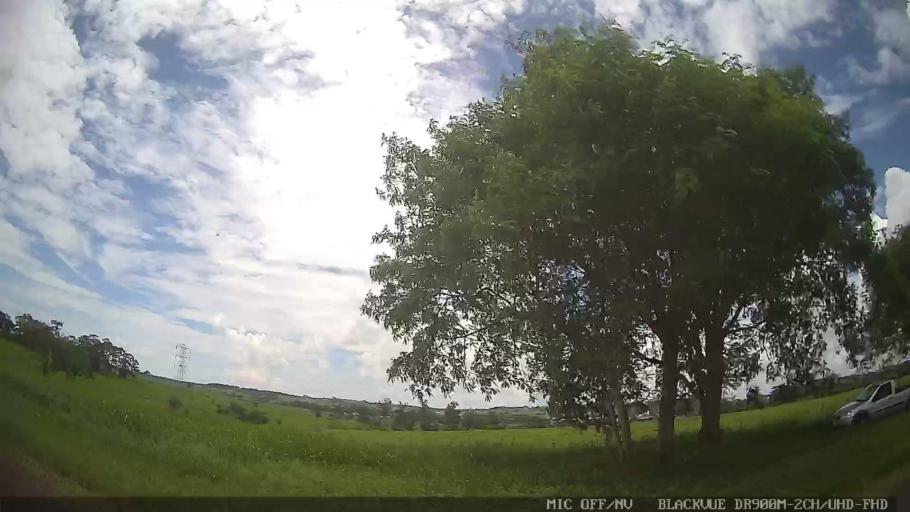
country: BR
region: Sao Paulo
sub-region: Conchas
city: Conchas
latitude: -23.0455
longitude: -47.9479
